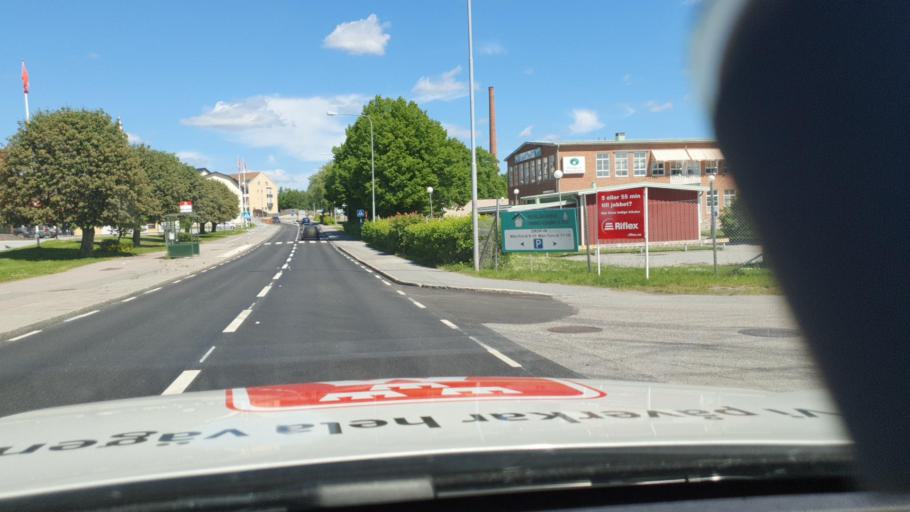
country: SE
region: Stockholm
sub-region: Norrtalje Kommun
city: Rimbo
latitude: 59.7406
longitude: 18.3700
